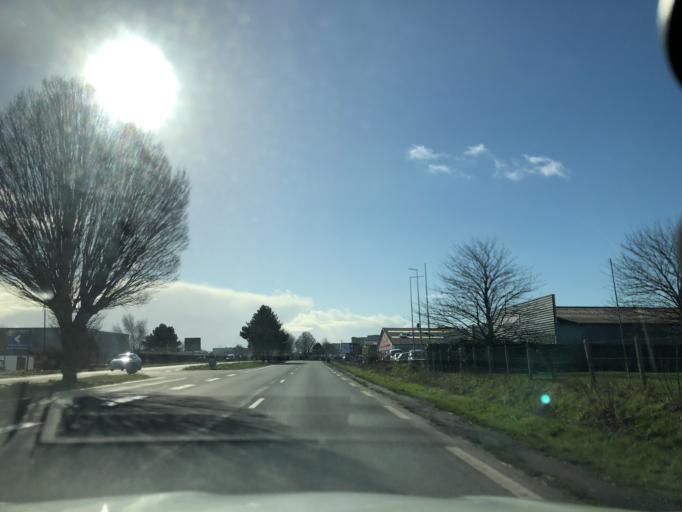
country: FR
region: Lower Normandy
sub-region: Departement du Calvados
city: Caen
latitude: 49.2102
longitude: -0.3450
